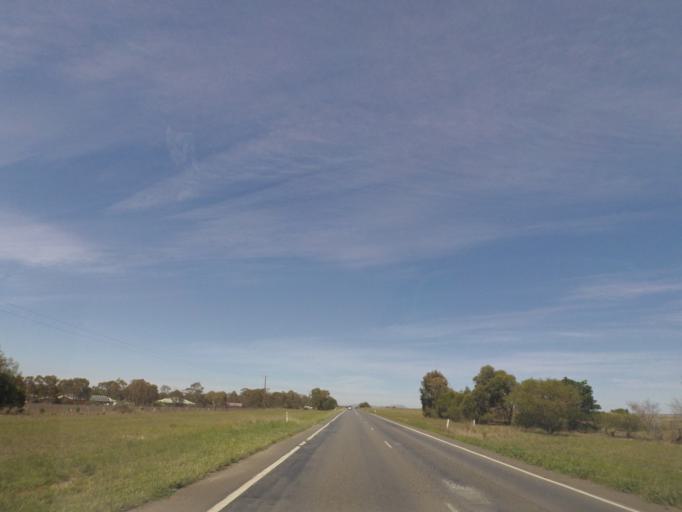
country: AU
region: Victoria
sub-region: Moorabool
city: Bacchus Marsh
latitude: -37.7856
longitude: 144.4254
